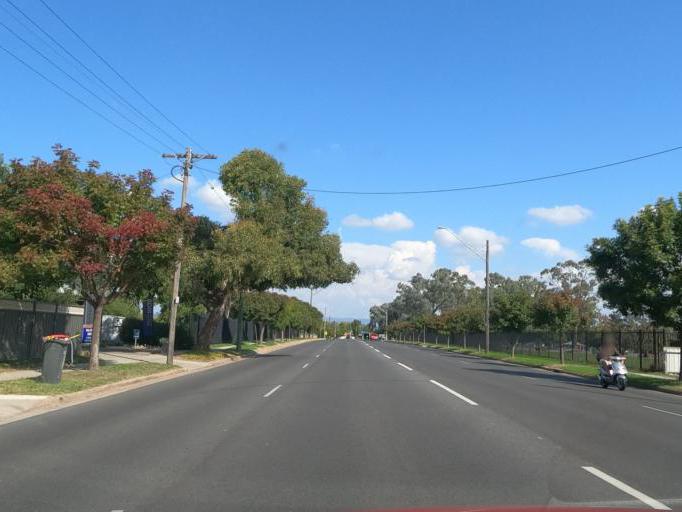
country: AU
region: New South Wales
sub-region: Albury Municipality
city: North Albury
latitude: -36.0595
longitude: 146.9267
